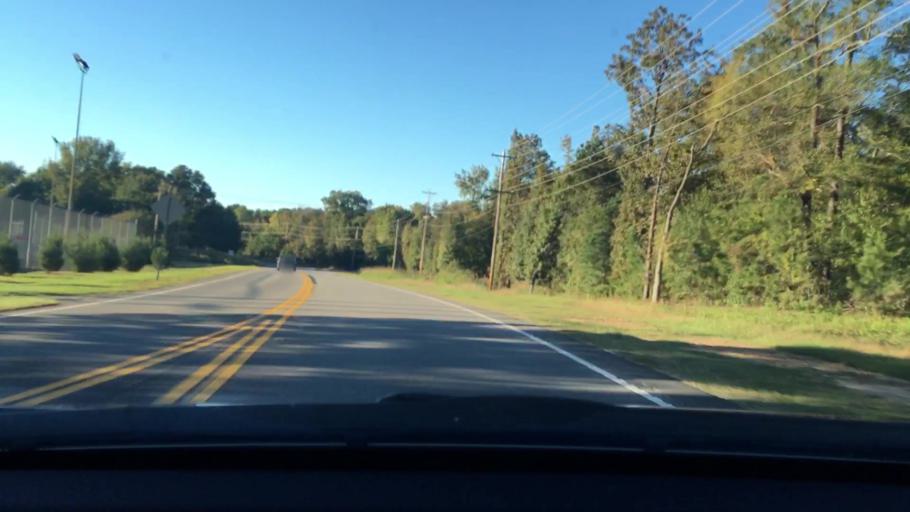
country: US
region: South Carolina
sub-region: Lexington County
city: Irmo
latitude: 34.0994
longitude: -81.1676
